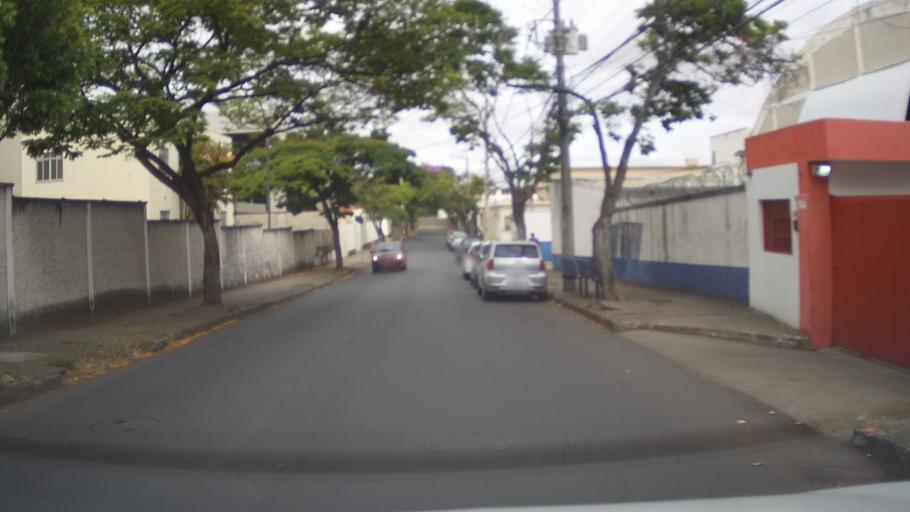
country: BR
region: Minas Gerais
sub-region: Belo Horizonte
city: Belo Horizonte
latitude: -19.8529
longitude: -43.9531
